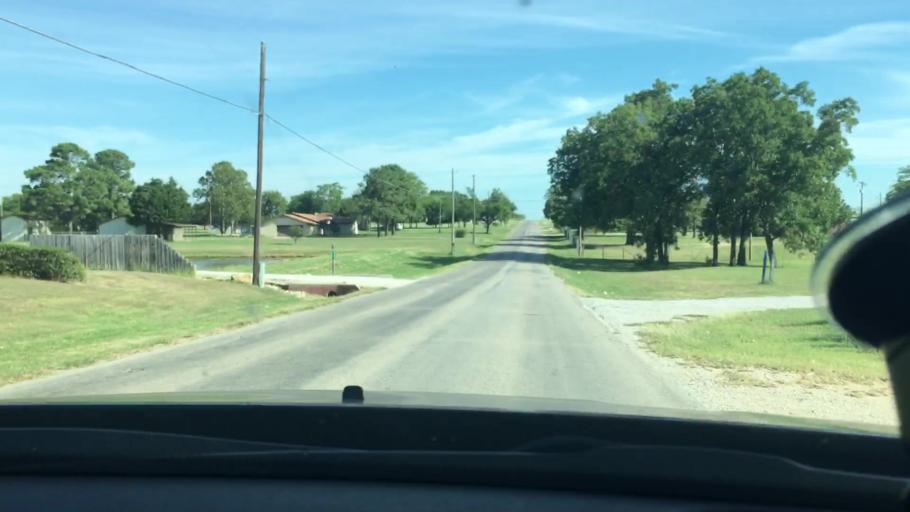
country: US
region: Oklahoma
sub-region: Carter County
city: Lone Grove
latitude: 34.1820
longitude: -97.2475
